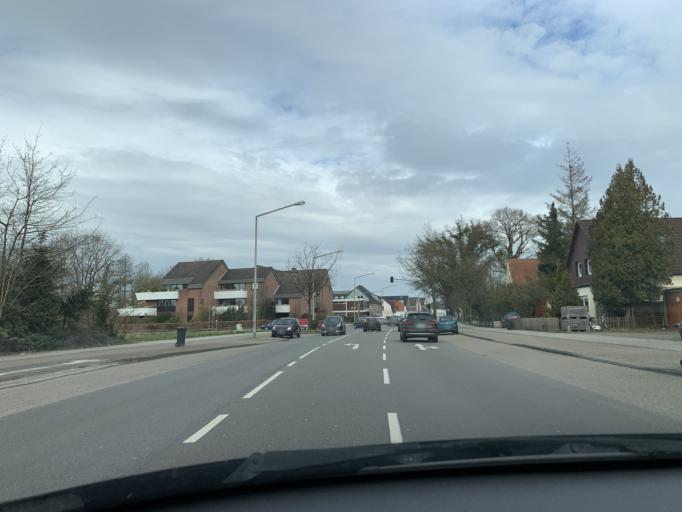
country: DE
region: Lower Saxony
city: Oldenburg
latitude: 53.1277
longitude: 8.1901
